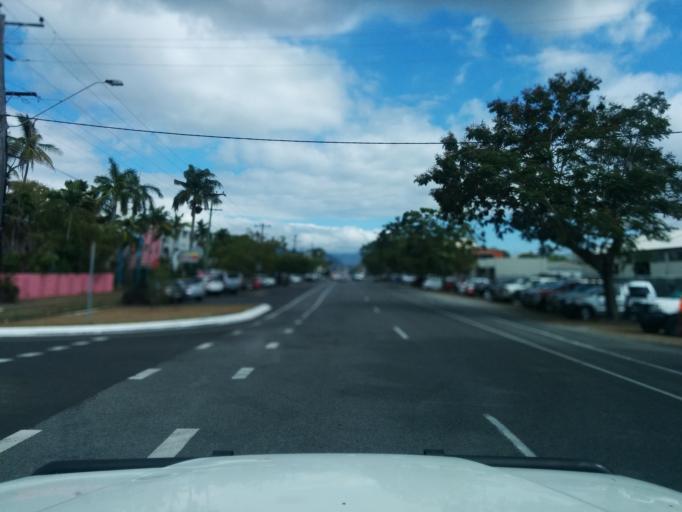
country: AU
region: Queensland
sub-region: Cairns
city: Cairns
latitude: -16.9160
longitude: 145.7654
